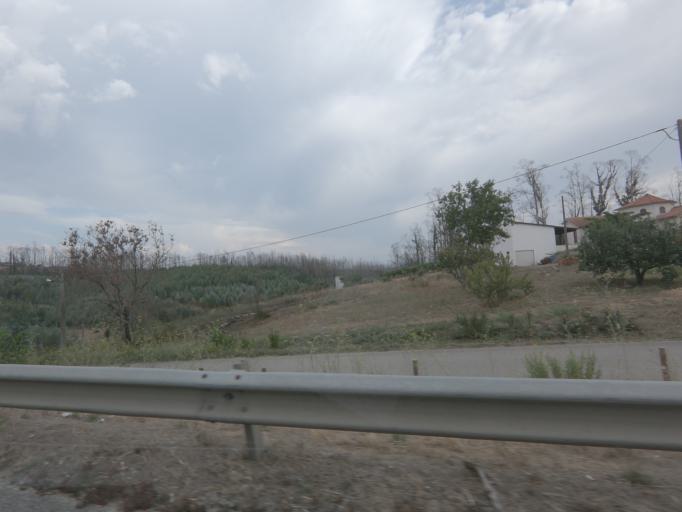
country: PT
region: Viseu
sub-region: Santa Comba Dao
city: Santa Comba Dao
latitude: 40.3560
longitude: -8.1454
